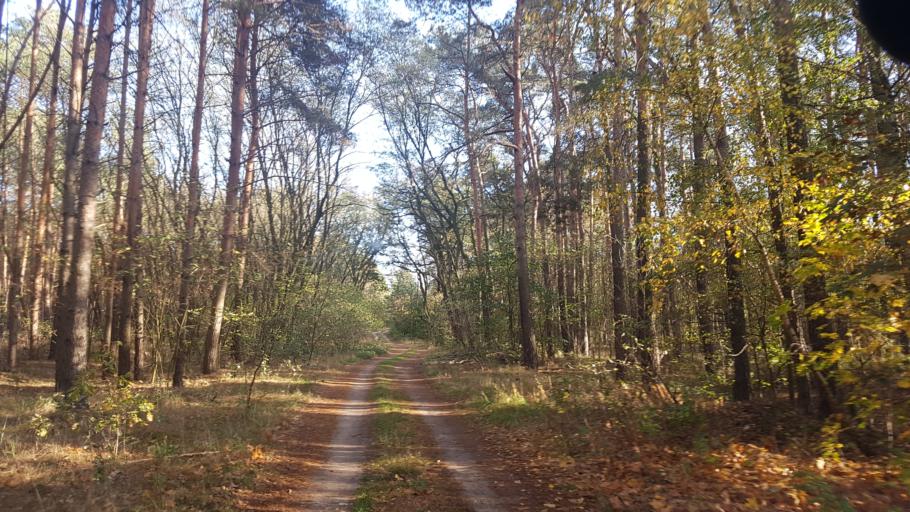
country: DE
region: Brandenburg
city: Schonewalde
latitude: 51.6534
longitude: 13.6196
